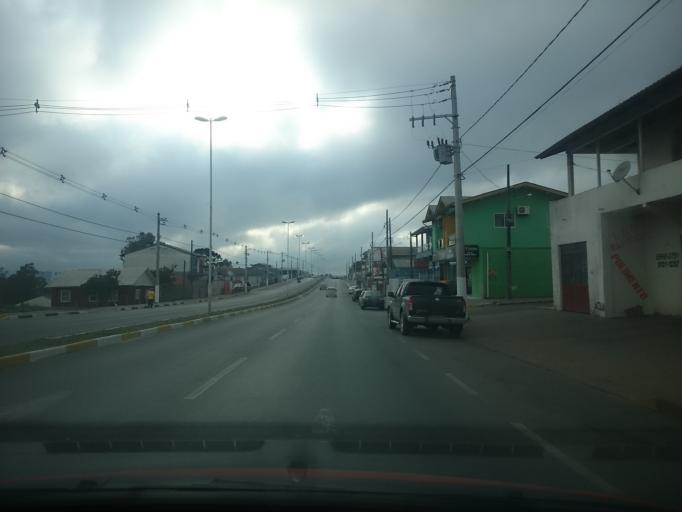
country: BR
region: Santa Catarina
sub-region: Lages
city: Lages
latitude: -27.8310
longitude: -50.3437
